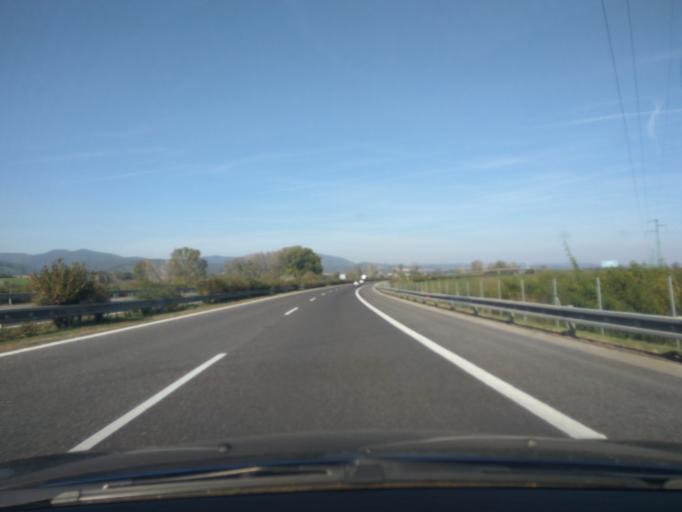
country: SK
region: Trenciansky
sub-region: Okres Nove Mesto nad Vahom
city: Nove Mesto nad Vahom
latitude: 48.8160
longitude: 17.9070
